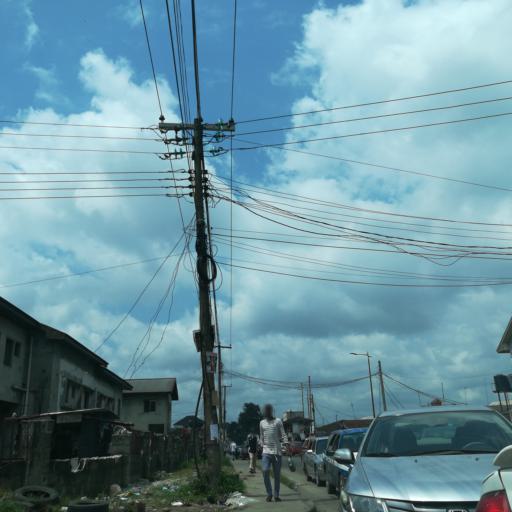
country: NG
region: Rivers
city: Port Harcourt
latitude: 4.8044
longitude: 7.0050
